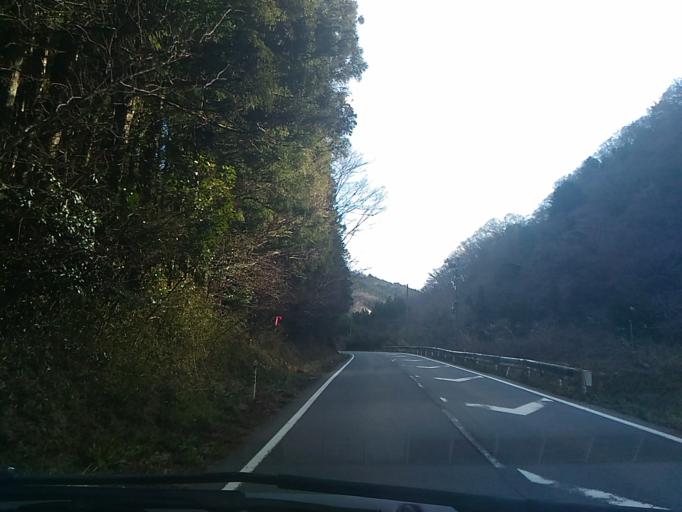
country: JP
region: Fukushima
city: Iwaki
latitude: 37.0199
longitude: 140.6643
